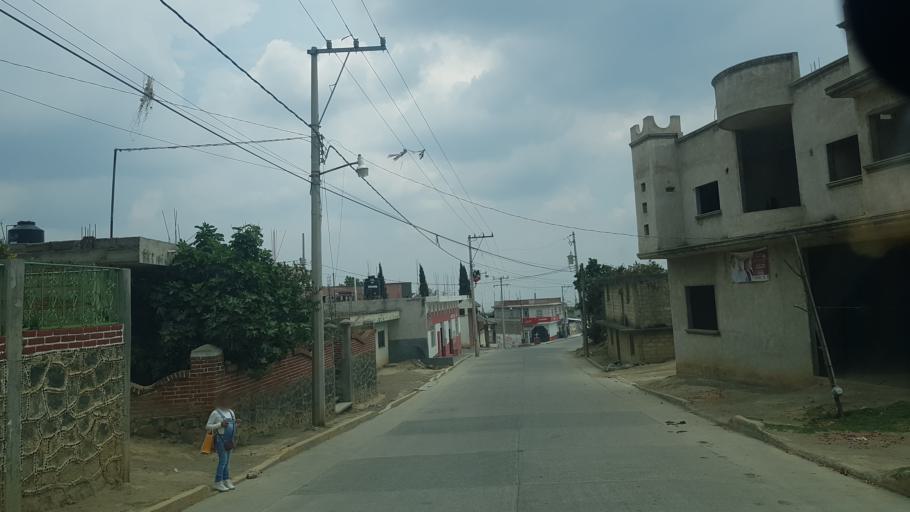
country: MX
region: Puebla
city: Domingo Arenas
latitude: 19.1525
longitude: -98.5020
